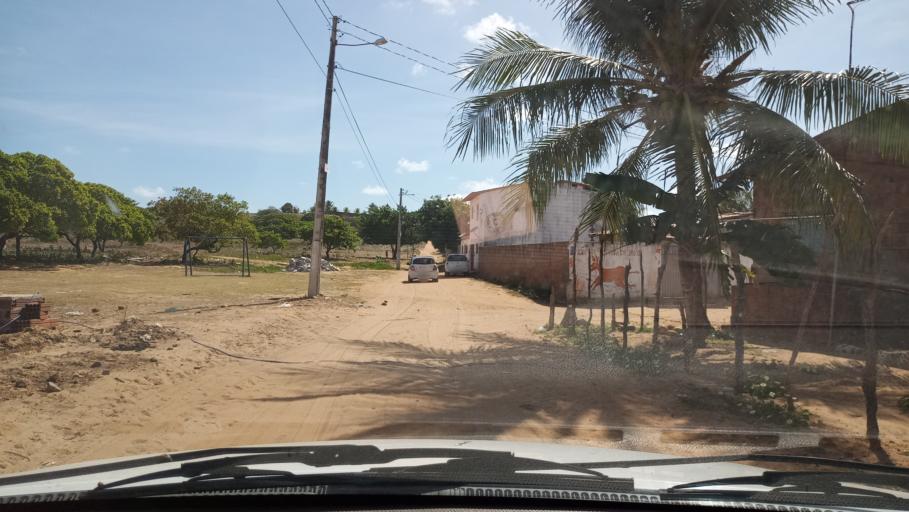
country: BR
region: Rio Grande do Norte
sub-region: Maxaranguape
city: Sao Miguel
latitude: -5.5134
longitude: -35.2659
